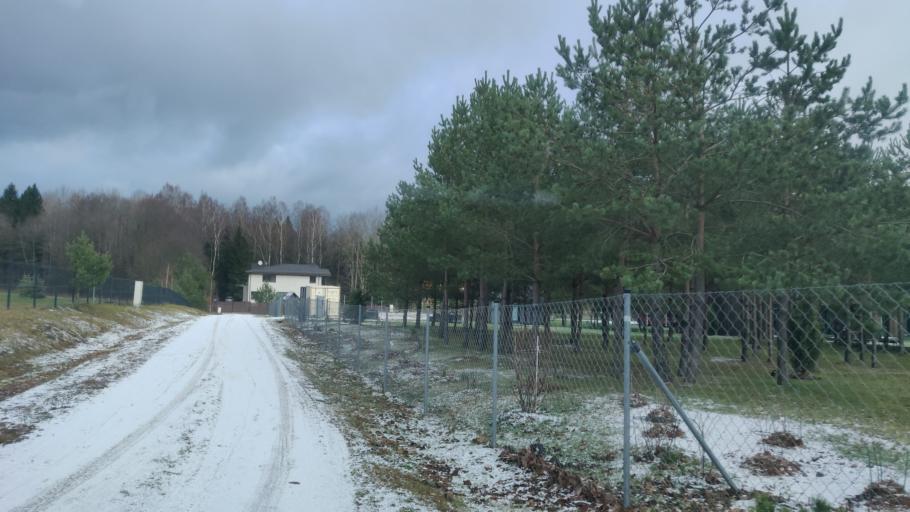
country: LT
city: Trakai
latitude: 54.5542
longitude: 24.9277
